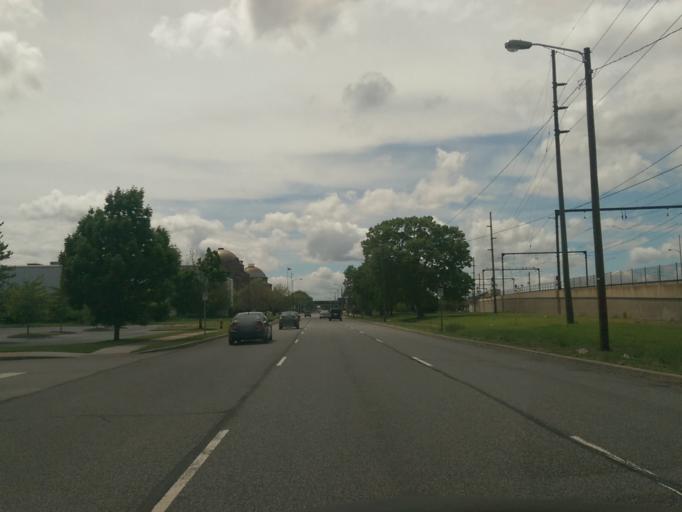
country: US
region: Indiana
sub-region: Lake County
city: Gary
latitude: 41.6039
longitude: -87.3330
